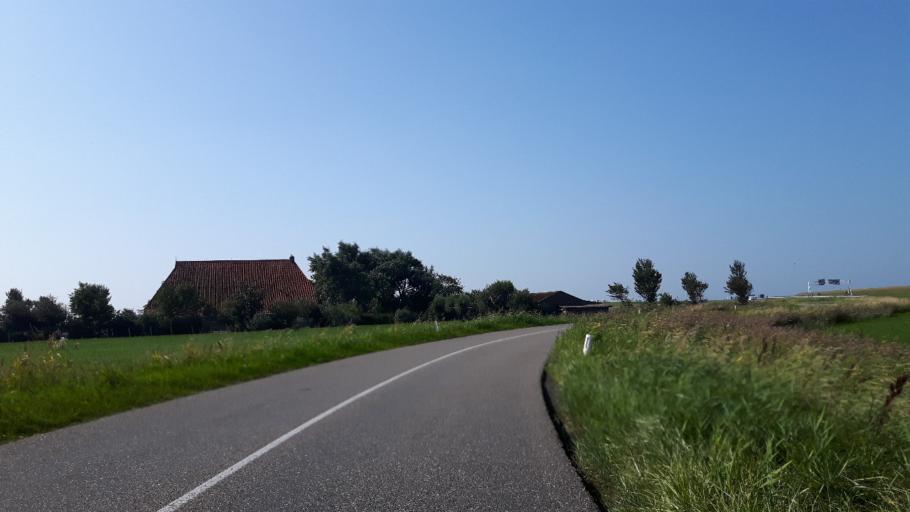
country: NL
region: Friesland
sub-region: Sudwest Fryslan
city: Makkum
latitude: 53.0938
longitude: 5.3831
